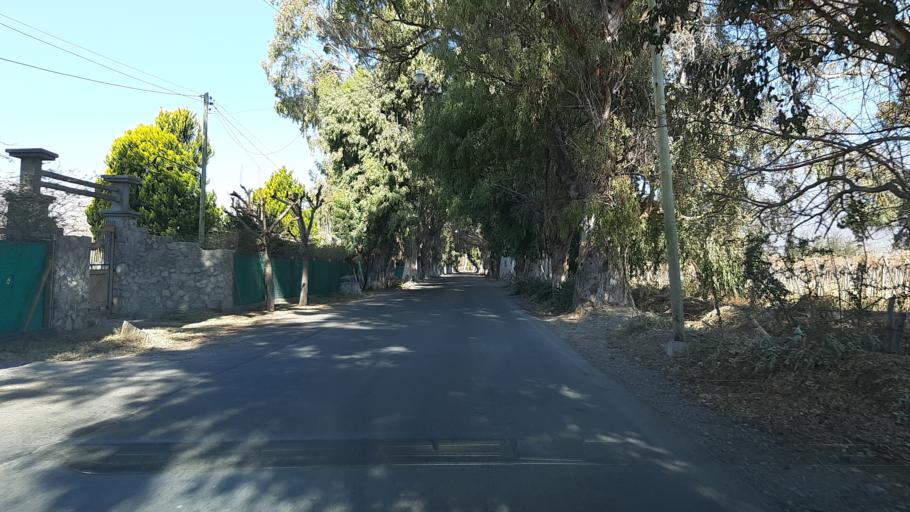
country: AR
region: San Juan
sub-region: Departamento de Zonda
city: Zonda
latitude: -31.5569
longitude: -68.7300
